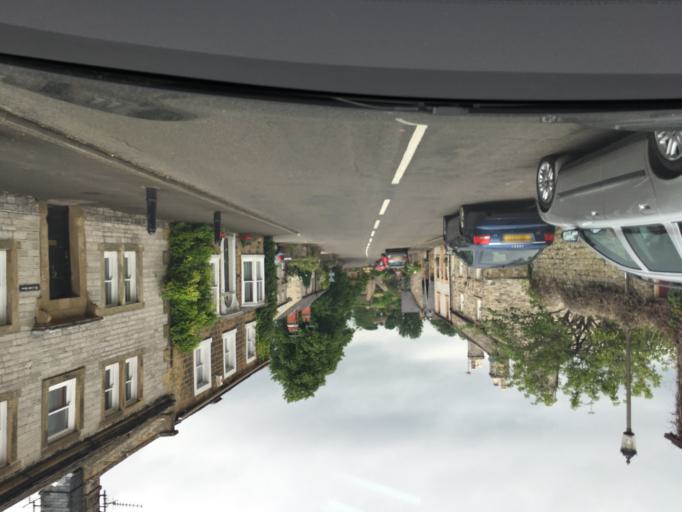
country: GB
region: England
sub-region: Derbyshire
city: Bakewell
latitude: 53.2246
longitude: -1.7069
